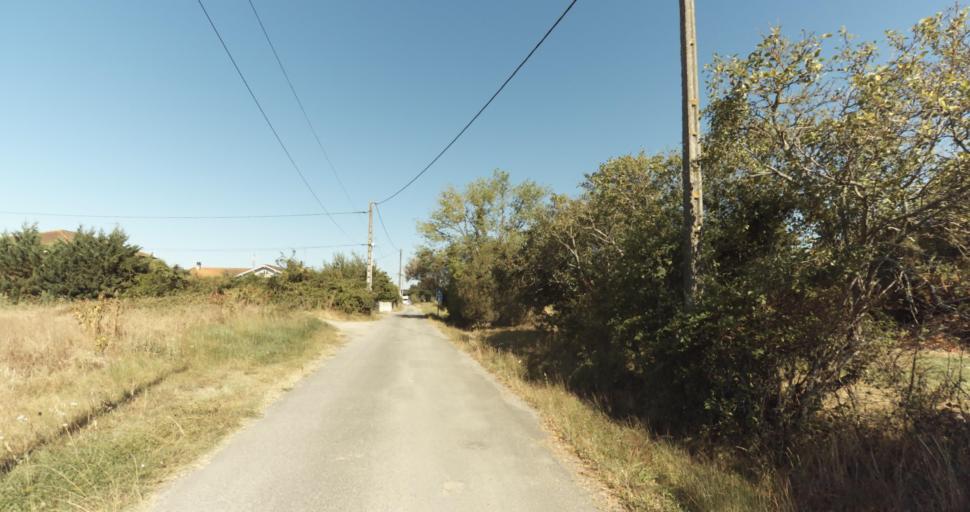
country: FR
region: Midi-Pyrenees
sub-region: Departement de la Haute-Garonne
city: Launaguet
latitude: 43.6616
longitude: 1.4642
